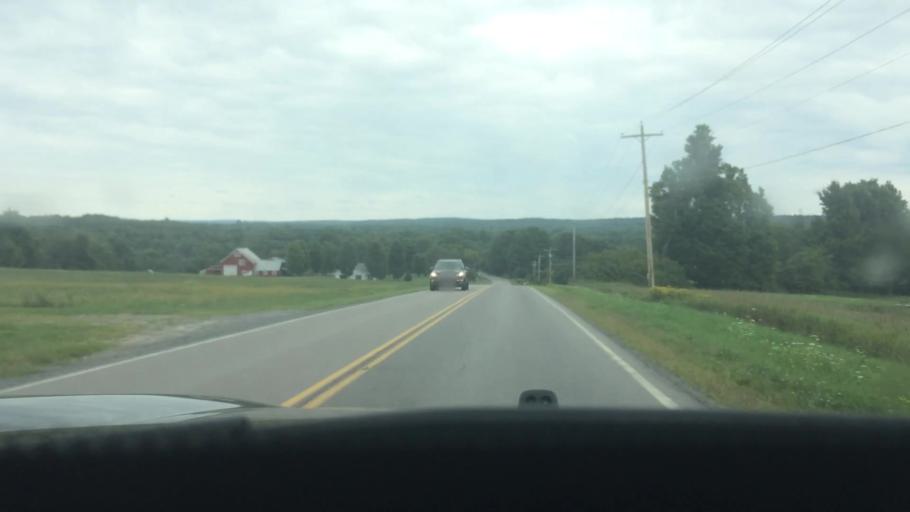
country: US
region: New York
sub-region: St. Lawrence County
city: Canton
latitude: 44.5399
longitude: -75.0800
